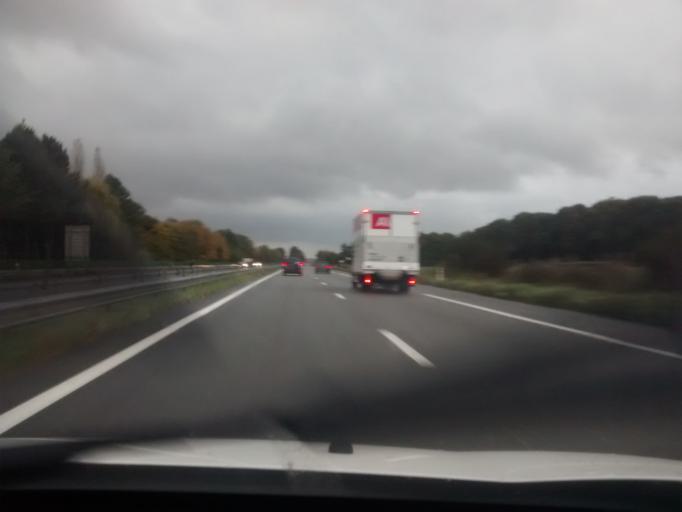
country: FR
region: Brittany
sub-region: Departement d'Ille-et-Vilaine
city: Saint-Pierre-de-Plesguen
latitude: 48.4794
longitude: -1.9097
